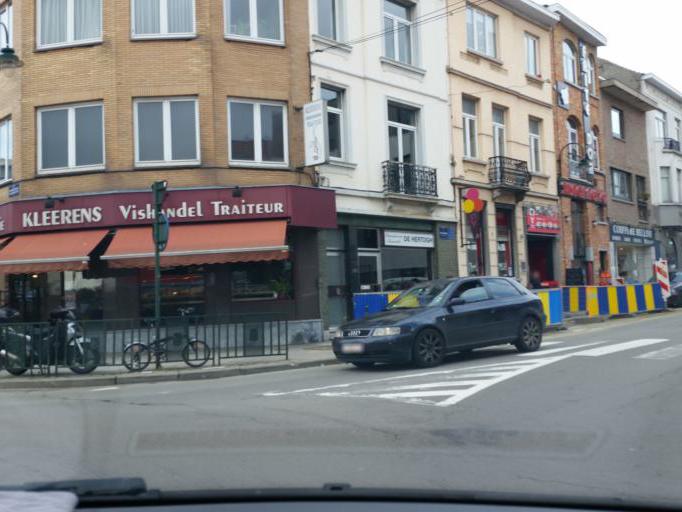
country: BE
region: Flanders
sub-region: Provincie Vlaams-Brabant
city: Grimbergen
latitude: 50.8994
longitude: 4.3601
